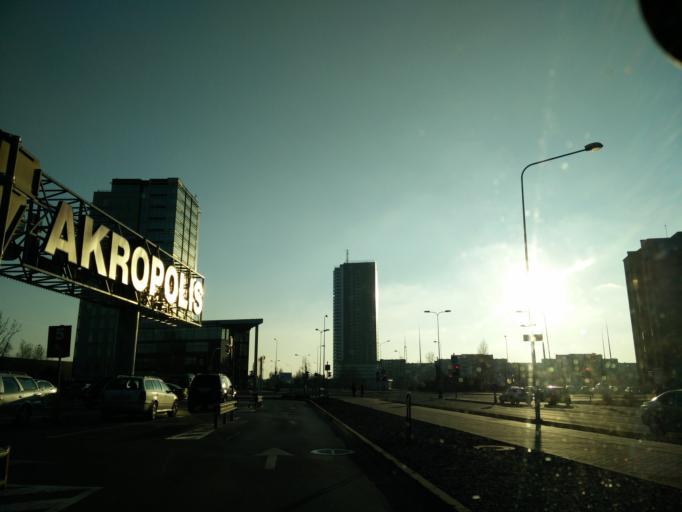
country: LT
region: Klaipedos apskritis
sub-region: Klaipeda
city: Klaipeda
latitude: 55.6938
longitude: 21.1531
